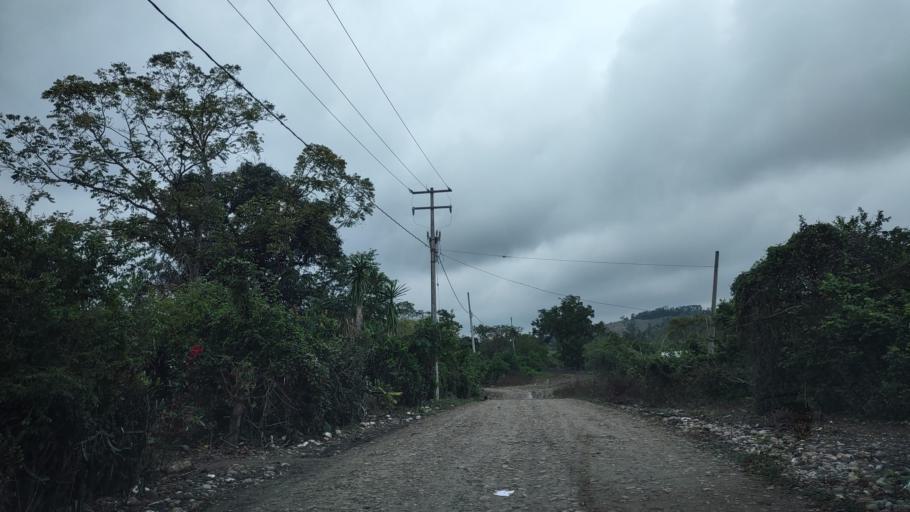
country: MX
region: Veracruz
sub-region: Coatzintla
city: Manuel Maria Contreras
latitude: 20.4053
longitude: -97.4534
